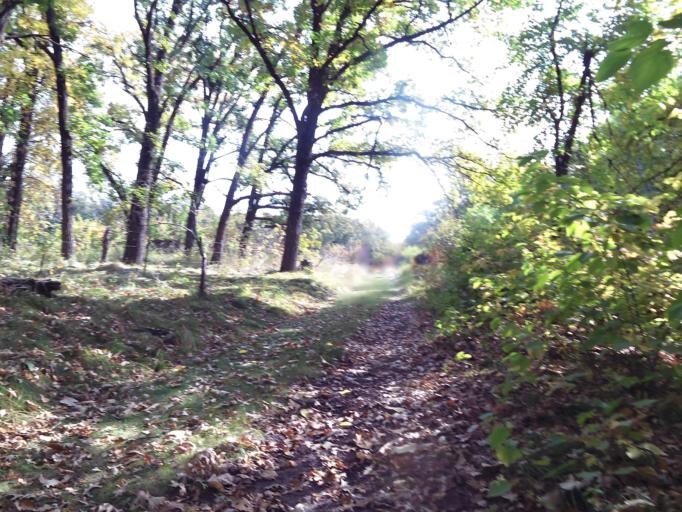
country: US
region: North Dakota
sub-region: Pembina County
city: Cavalier
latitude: 48.7799
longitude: -97.7351
